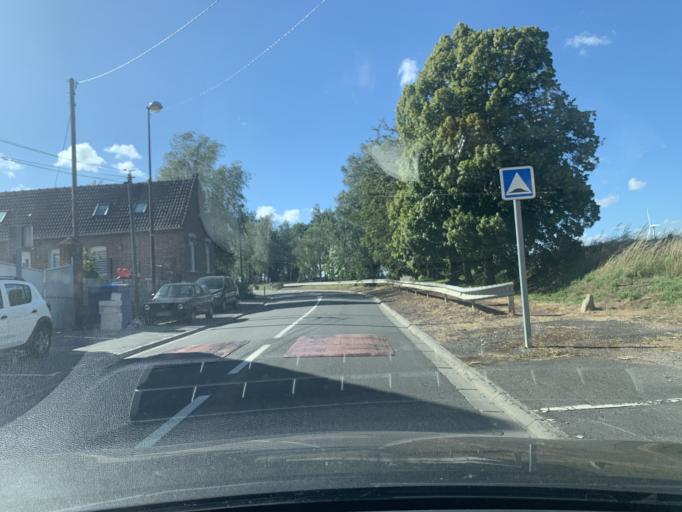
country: FR
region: Nord-Pas-de-Calais
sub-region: Departement du Nord
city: Lauwin-Planque
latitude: 50.3784
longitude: 3.0118
